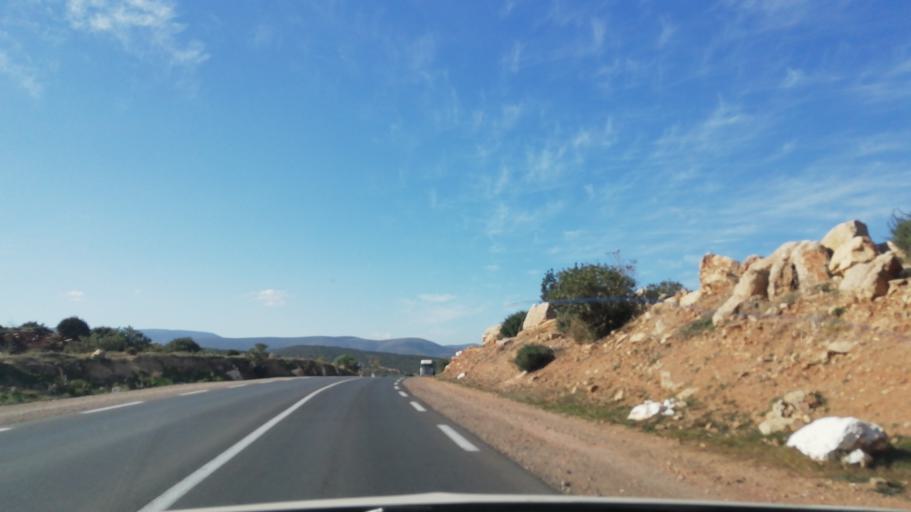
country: DZ
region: Tlemcen
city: Ouled Mimoun
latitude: 34.8690
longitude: -1.1296
